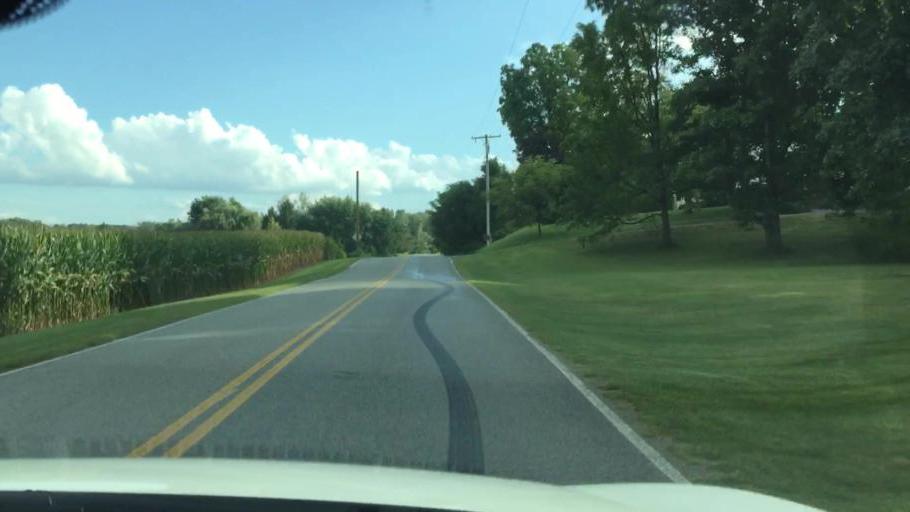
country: US
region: Ohio
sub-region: Champaign County
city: Mechanicsburg
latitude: 40.0634
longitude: -83.5890
